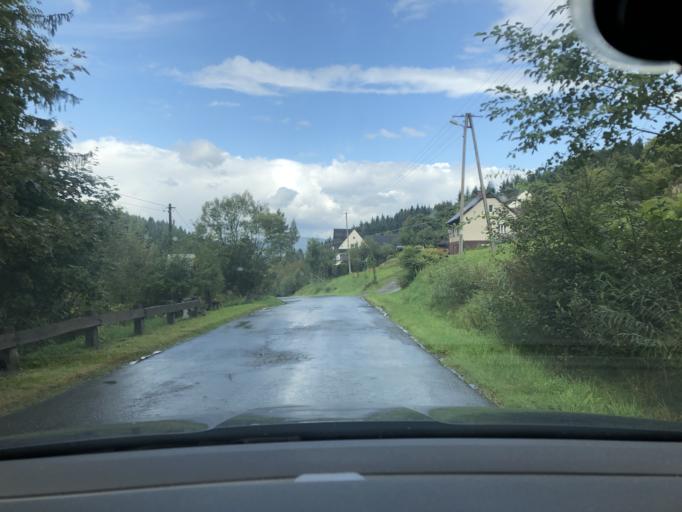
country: PL
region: Lesser Poland Voivodeship
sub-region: Powiat suski
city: Stryszawa
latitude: 49.6974
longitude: 19.5454
